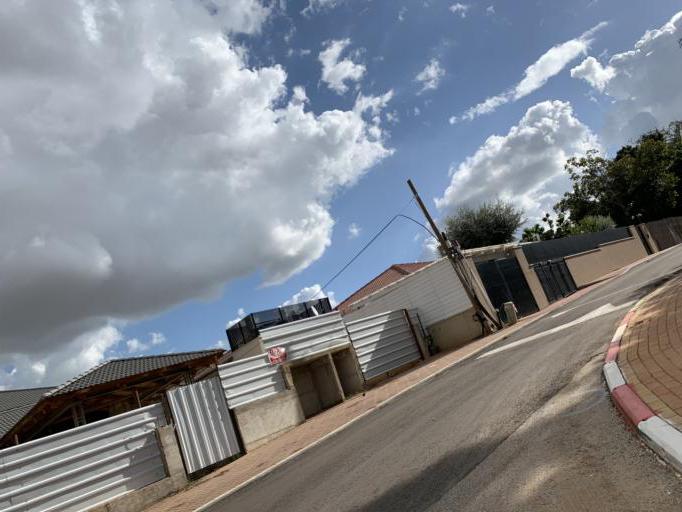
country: IL
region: Central District
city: Hod HaSharon
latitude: 32.1709
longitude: 34.8895
